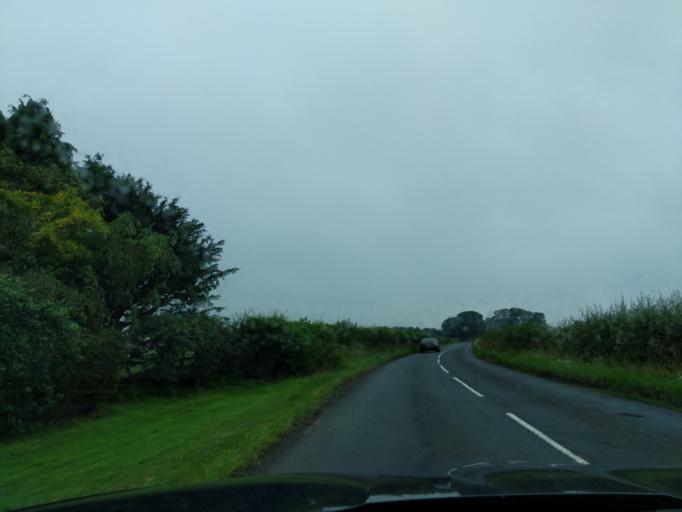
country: GB
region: England
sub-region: Northumberland
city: Lowick
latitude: 55.6552
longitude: -1.9138
